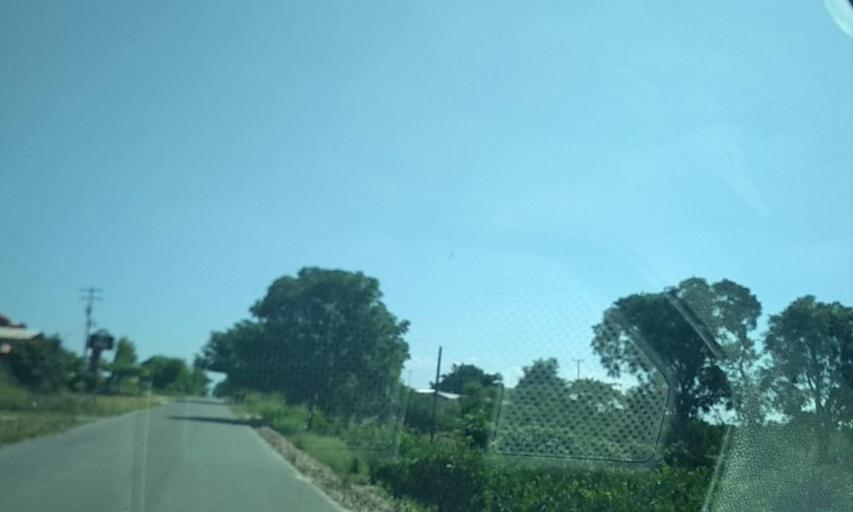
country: MX
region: Veracruz
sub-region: Martinez de la Torre
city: La Union Paso Largo
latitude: 20.1500
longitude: -97.0007
